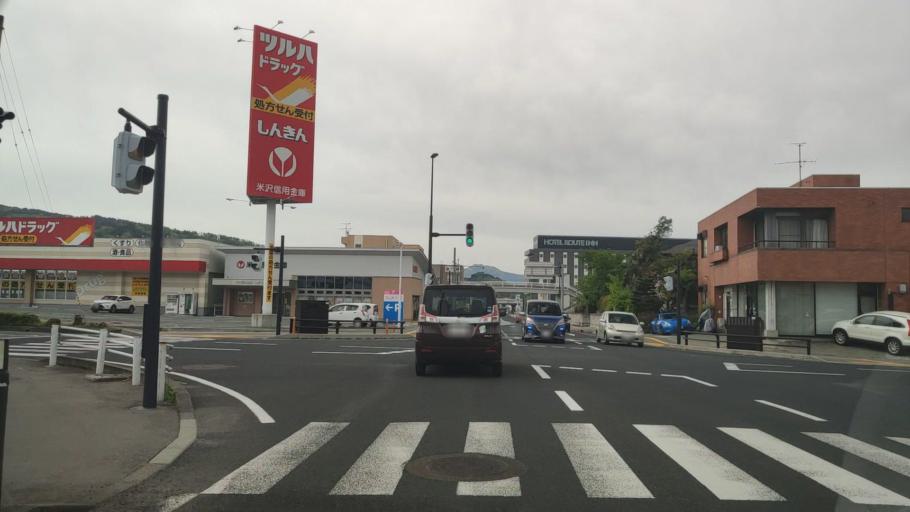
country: JP
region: Yamagata
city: Yamagata-shi
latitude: 38.2186
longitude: 140.3240
